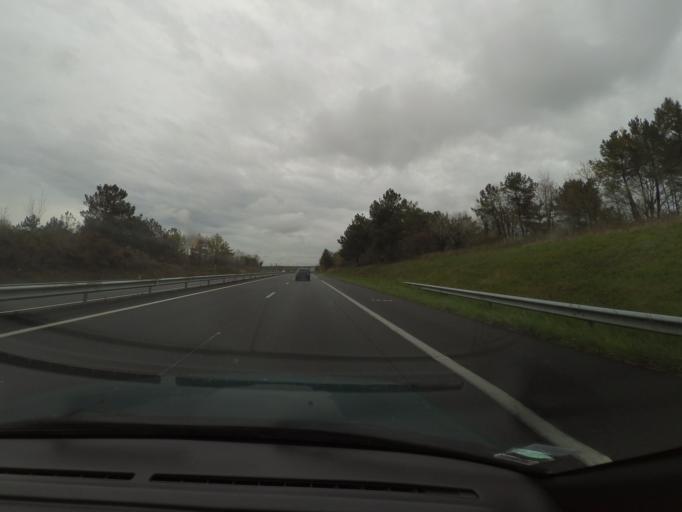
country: FR
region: Pays de la Loire
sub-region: Departement de Maine-et-Loire
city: Durtal
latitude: 47.6376
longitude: -0.2746
